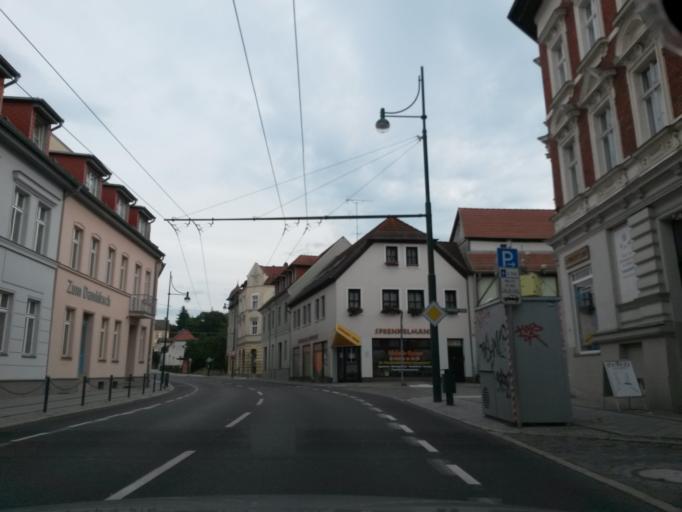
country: DE
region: Brandenburg
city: Eberswalde
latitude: 52.8326
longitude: 13.8221
